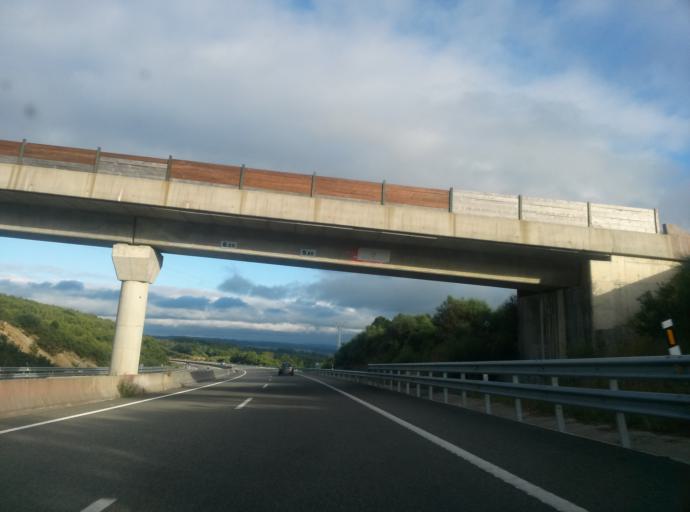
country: ES
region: Galicia
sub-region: Provincia de Lugo
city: Vilalba
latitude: 43.3648
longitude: -7.7764
